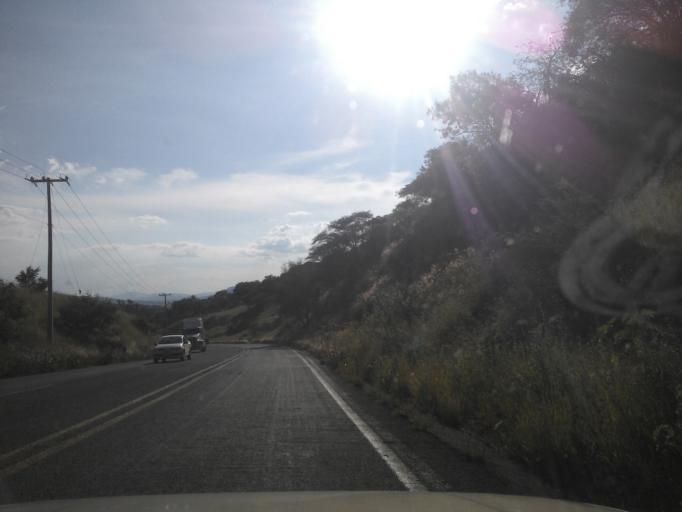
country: MX
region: Jalisco
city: Atotonilco el Alto
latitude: 20.5536
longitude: -102.5195
